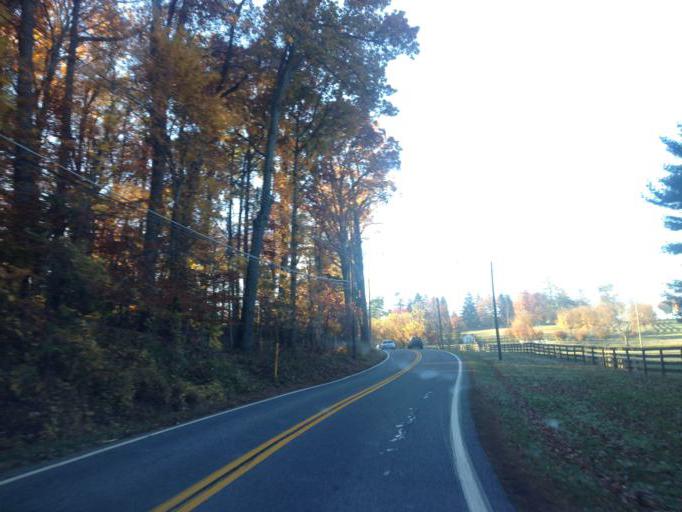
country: US
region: Maryland
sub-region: Baltimore County
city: Mays Chapel
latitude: 39.4098
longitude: -76.6856
